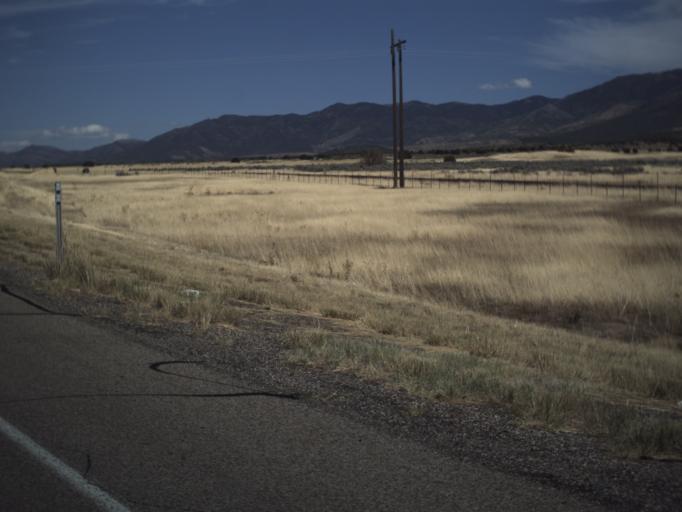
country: US
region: Utah
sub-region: Millard County
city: Fillmore
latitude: 38.9934
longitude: -112.3217
